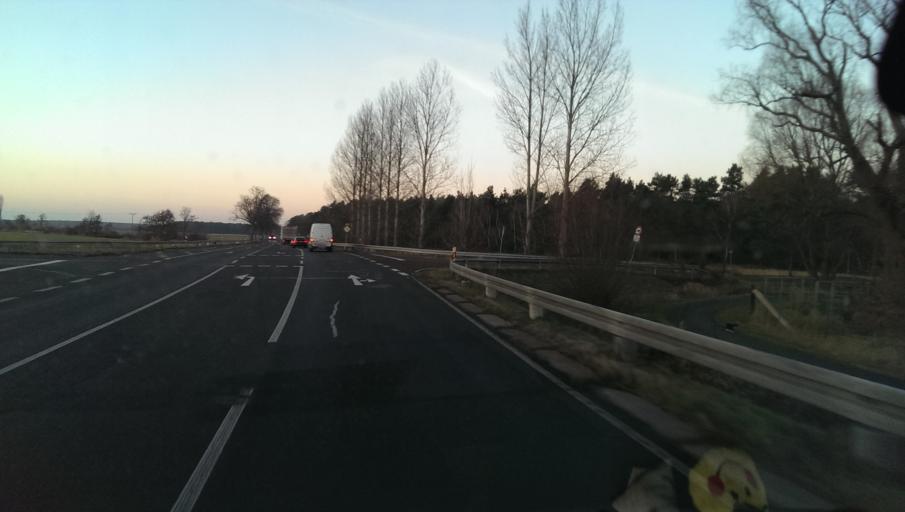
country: DE
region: Brandenburg
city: Herzberg
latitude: 51.7567
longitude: 13.2095
